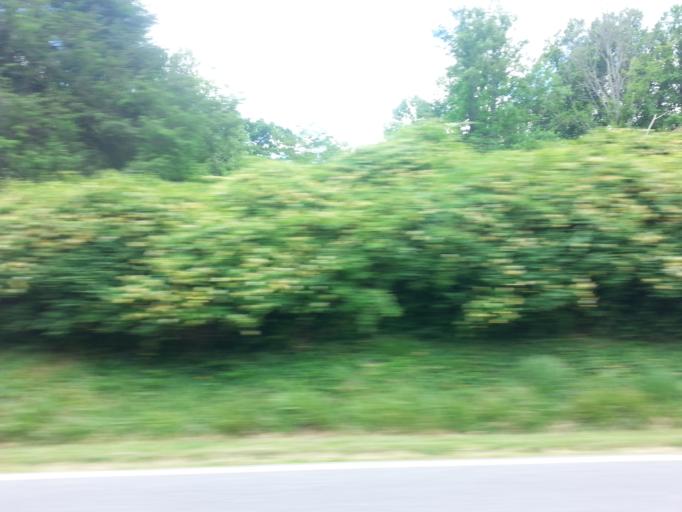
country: US
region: North Carolina
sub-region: Cherokee County
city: Andrews
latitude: 35.2139
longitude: -83.7558
